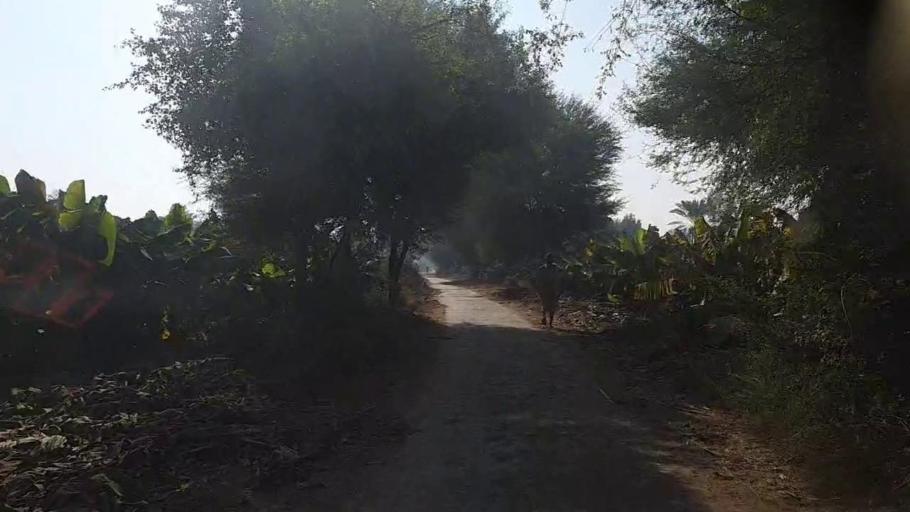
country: PK
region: Sindh
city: Kandiari
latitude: 27.0160
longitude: 68.5018
